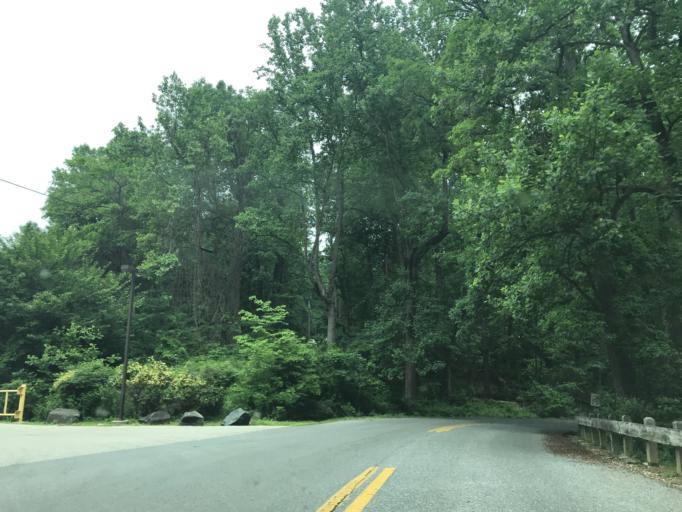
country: US
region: Maryland
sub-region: Howard County
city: Ellicott City
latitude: 39.2960
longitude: -76.7887
